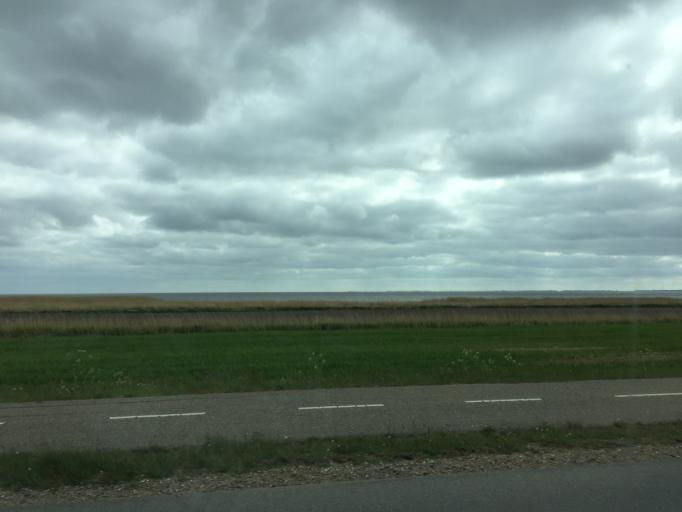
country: DK
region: Central Jutland
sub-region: Ringkobing-Skjern Kommune
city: Ringkobing
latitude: 56.0619
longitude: 8.2993
